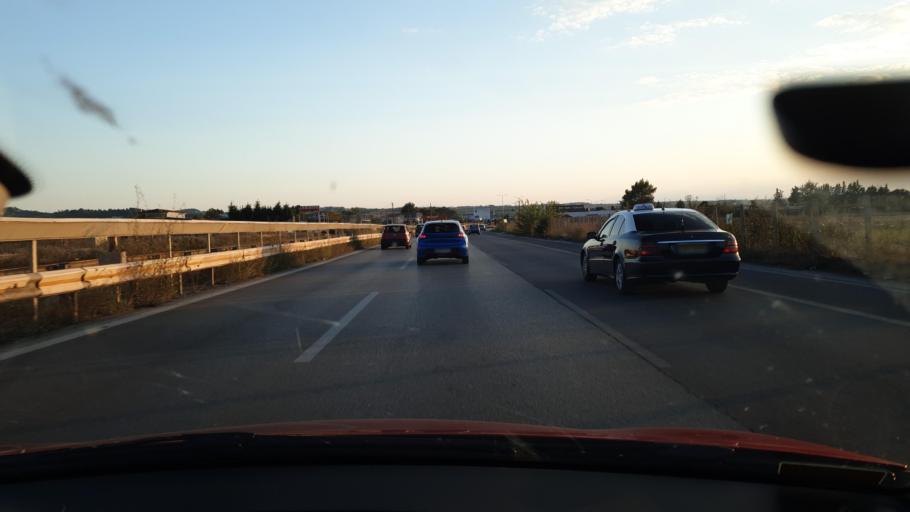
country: GR
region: Central Macedonia
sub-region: Nomos Thessalonikis
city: Neo Rysi
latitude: 40.5160
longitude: 22.9913
